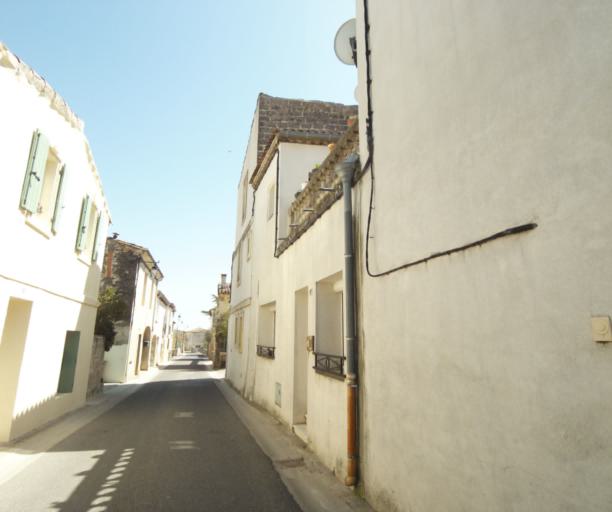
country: FR
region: Languedoc-Roussillon
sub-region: Departement de l'Herault
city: Beaulieu
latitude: 43.7288
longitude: 4.0212
